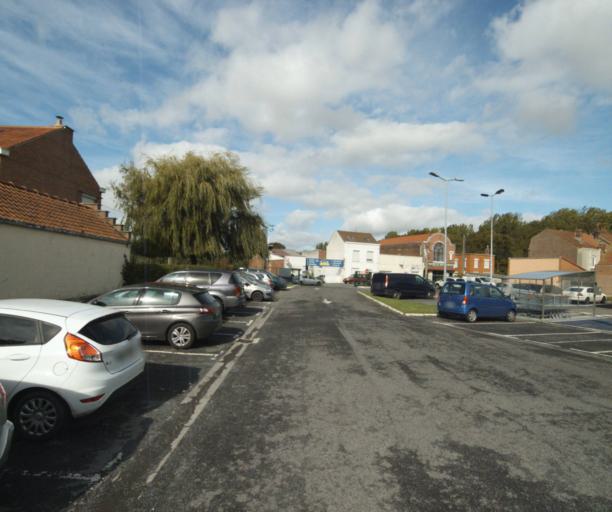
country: FR
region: Nord-Pas-de-Calais
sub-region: Departement du Nord
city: Houplines
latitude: 50.6905
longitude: 2.9092
